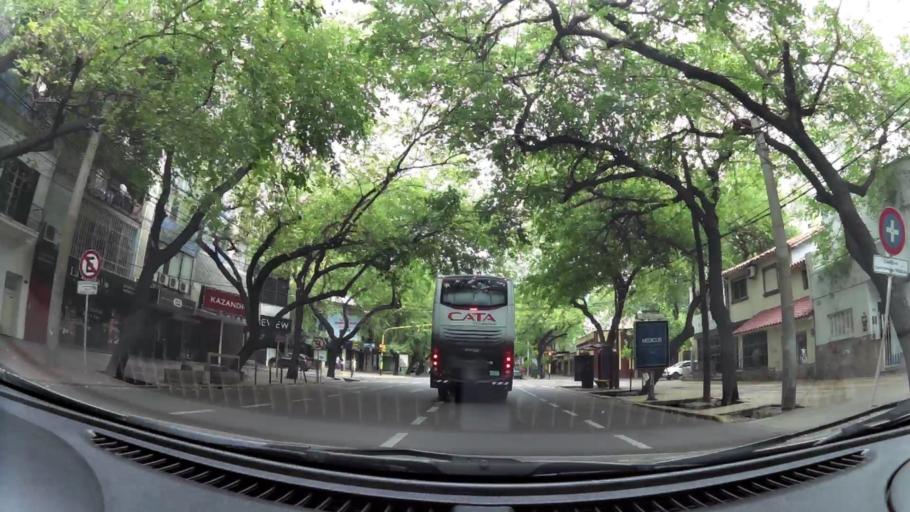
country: AR
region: Mendoza
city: Mendoza
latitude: -32.8936
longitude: -68.8479
